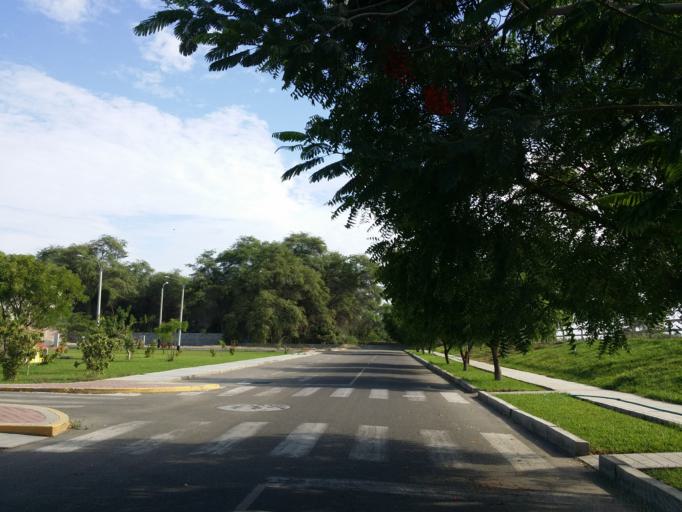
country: PE
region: Piura
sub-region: Provincia de Piura
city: Piura
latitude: -5.1741
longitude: -80.6235
